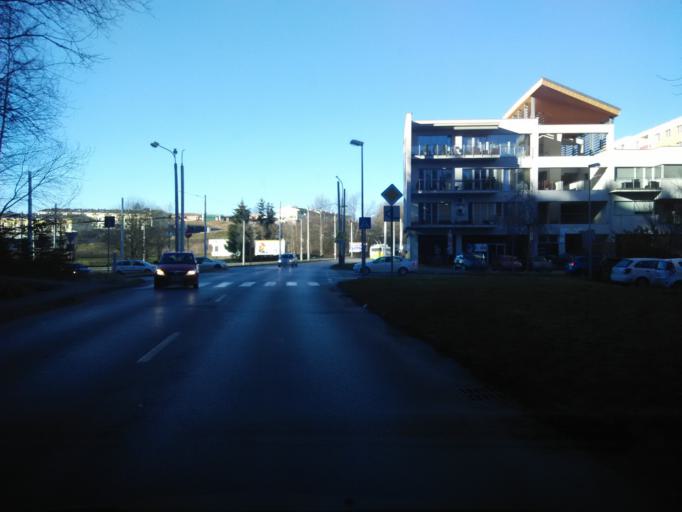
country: SK
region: Zilinsky
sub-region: Okres Zilina
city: Zilina
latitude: 49.2030
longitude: 18.7644
